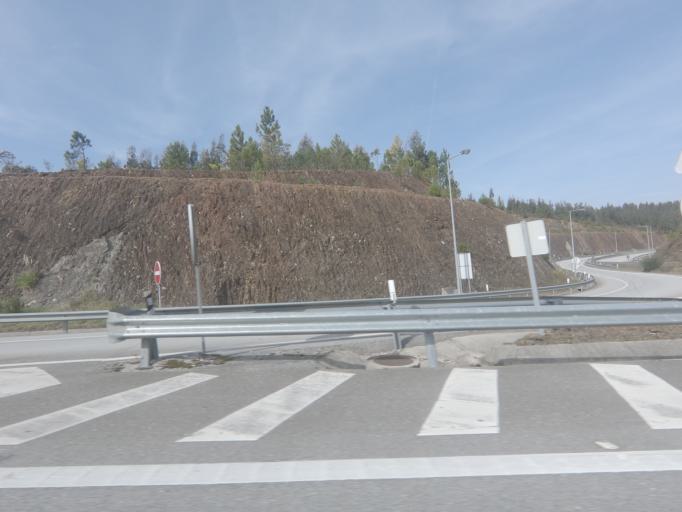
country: PT
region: Aveiro
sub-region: Albergaria-A-Velha
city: Albergaria-a-Velha
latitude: 40.6780
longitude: -8.4434
